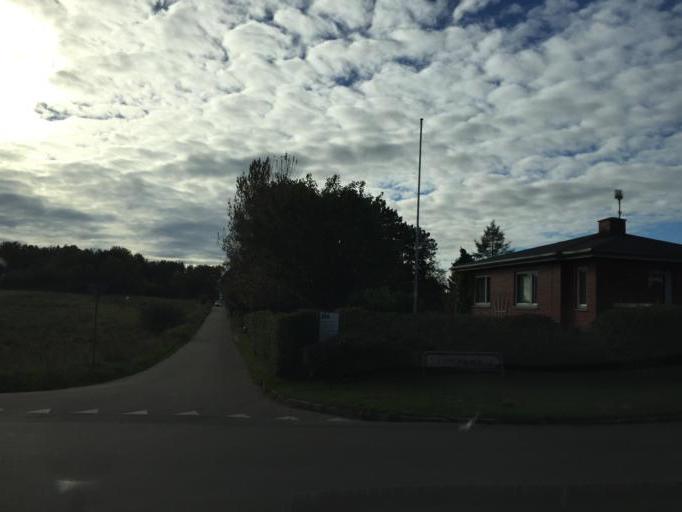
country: DK
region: Zealand
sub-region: Odsherred Kommune
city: Asnaes
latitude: 55.8379
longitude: 11.4517
